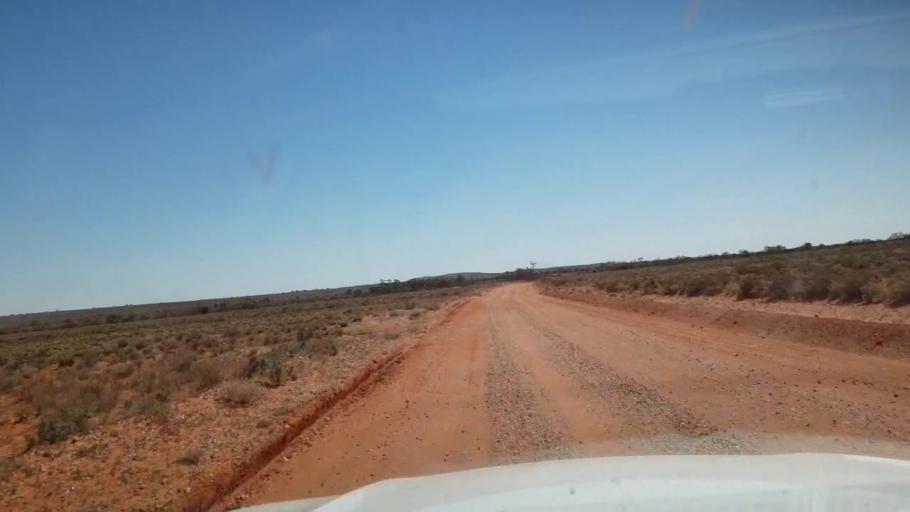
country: AU
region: South Australia
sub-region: Whyalla
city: Whyalla
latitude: -32.6859
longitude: 137.1129
